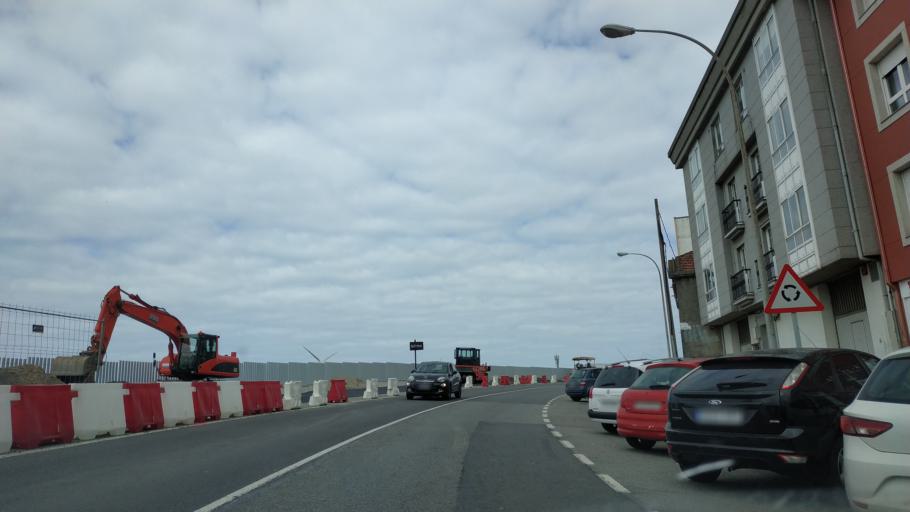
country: ES
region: Galicia
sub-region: Provincia da Coruna
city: Arteixo
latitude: 43.3129
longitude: -8.5012
